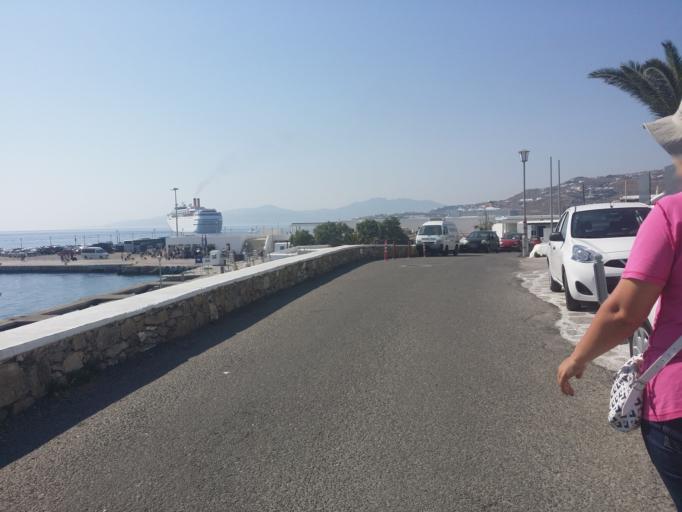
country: GR
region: South Aegean
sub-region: Nomos Kykladon
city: Mykonos
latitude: 37.4505
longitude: 25.3292
